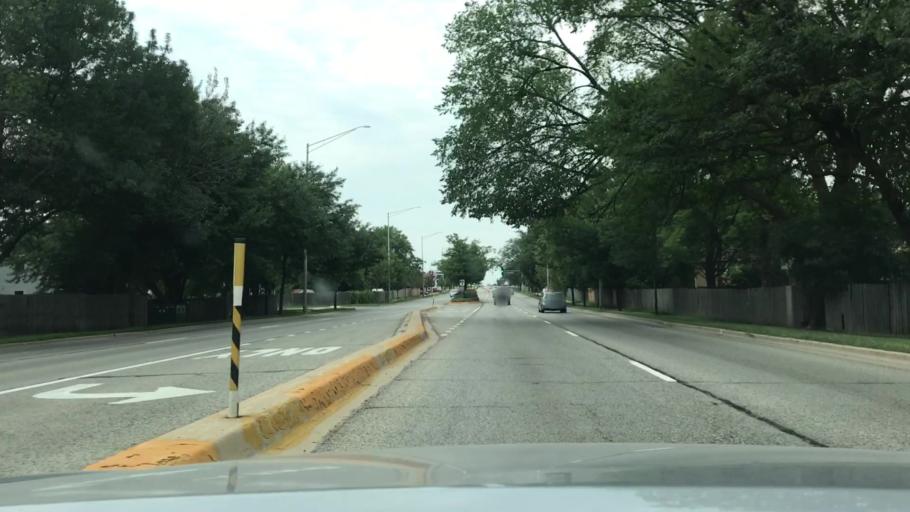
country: US
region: Illinois
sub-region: Will County
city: Bolingbrook
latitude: 41.7060
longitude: -88.0685
